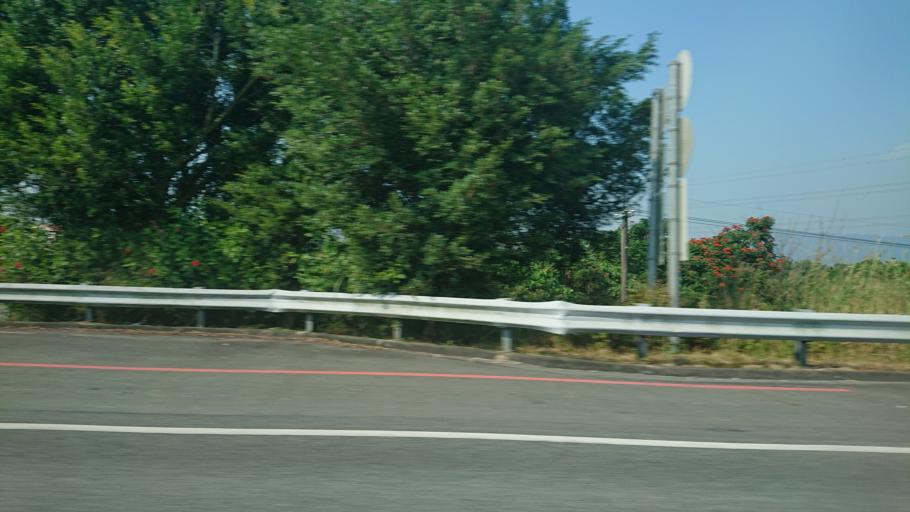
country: TW
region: Taiwan
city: Lugu
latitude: 23.7881
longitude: 120.7046
